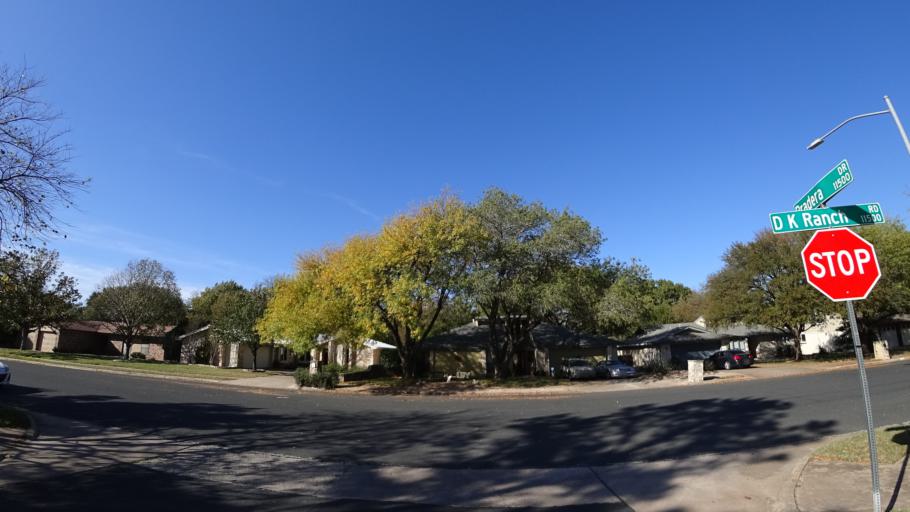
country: US
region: Texas
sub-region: Williamson County
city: Jollyville
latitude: 30.4269
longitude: -97.7731
